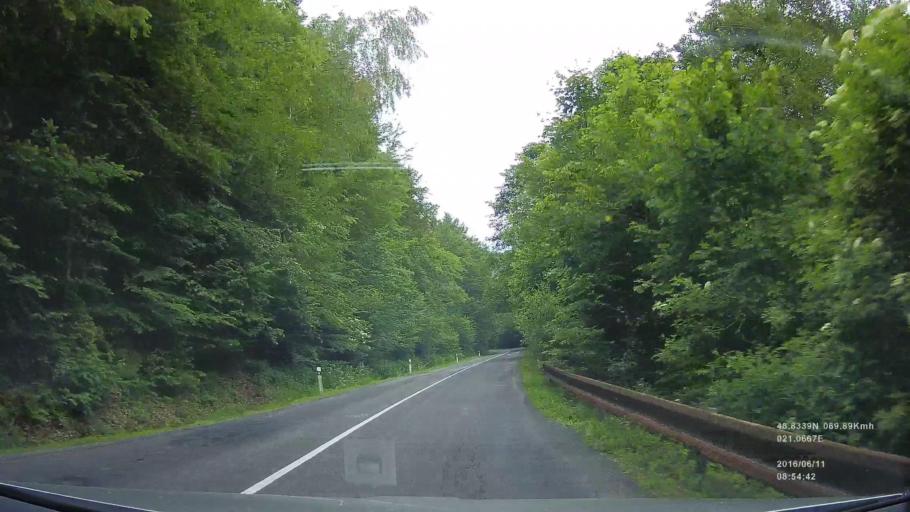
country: SK
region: Kosicky
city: Gelnica
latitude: 48.8049
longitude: 21.0998
